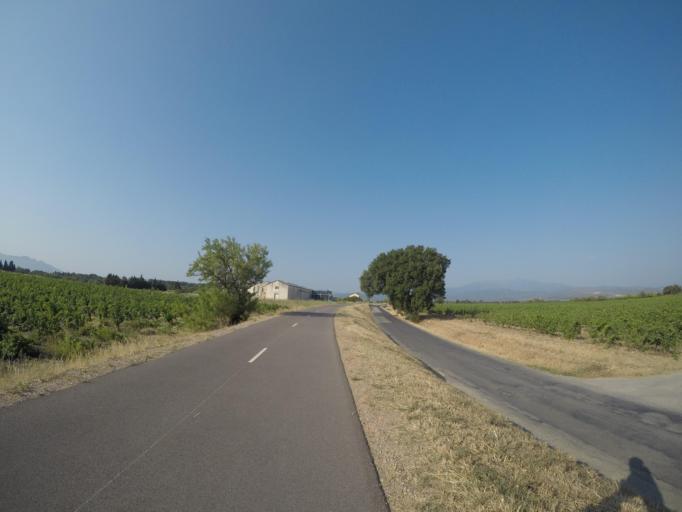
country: FR
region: Languedoc-Roussillon
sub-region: Departement des Pyrenees-Orientales
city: Ponteilla
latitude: 42.6303
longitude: 2.8056
